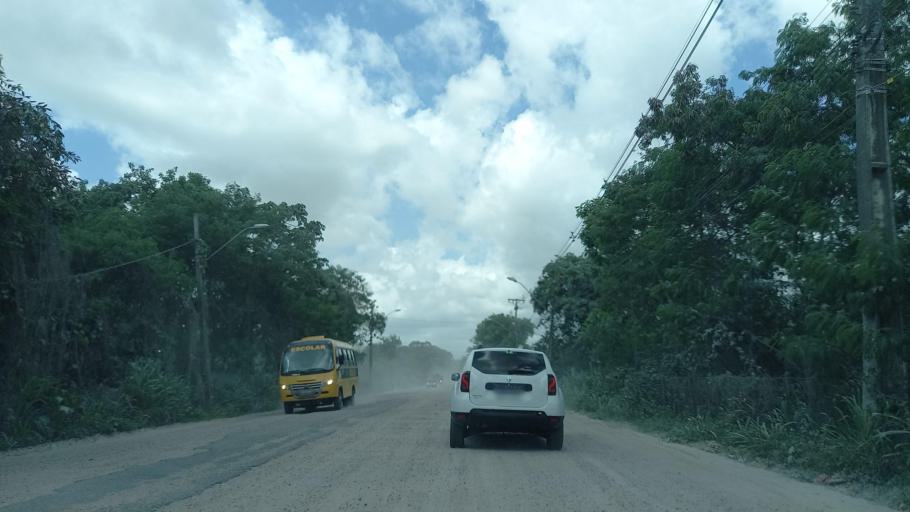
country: BR
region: Pernambuco
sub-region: Jaboatao Dos Guararapes
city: Jaboatao
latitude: -8.1588
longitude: -34.9772
